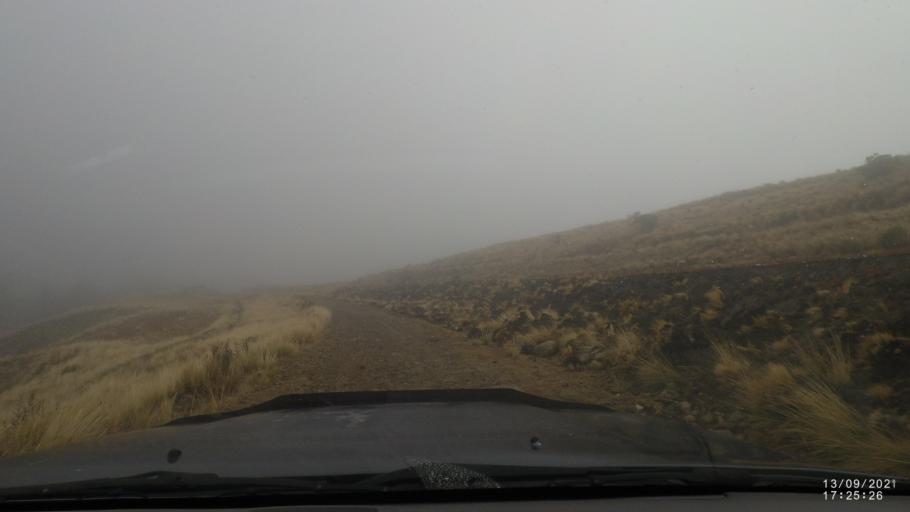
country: BO
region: Cochabamba
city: Colomi
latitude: -17.3583
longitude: -65.7811
